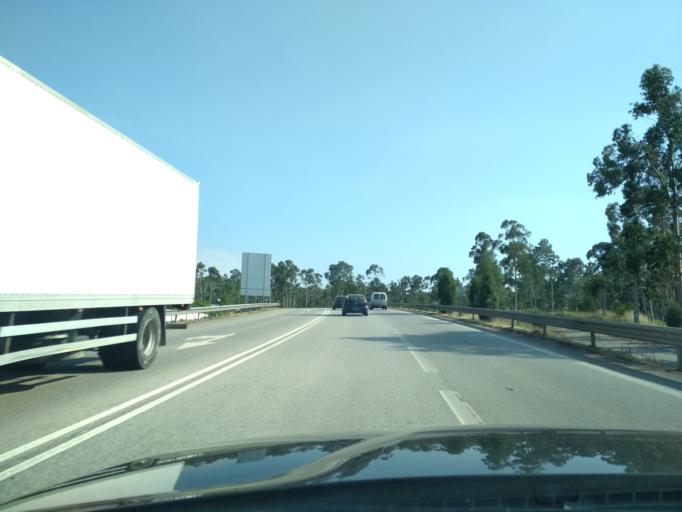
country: PT
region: Aveiro
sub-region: Mealhada
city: Mealhada
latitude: 40.3525
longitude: -8.4520
